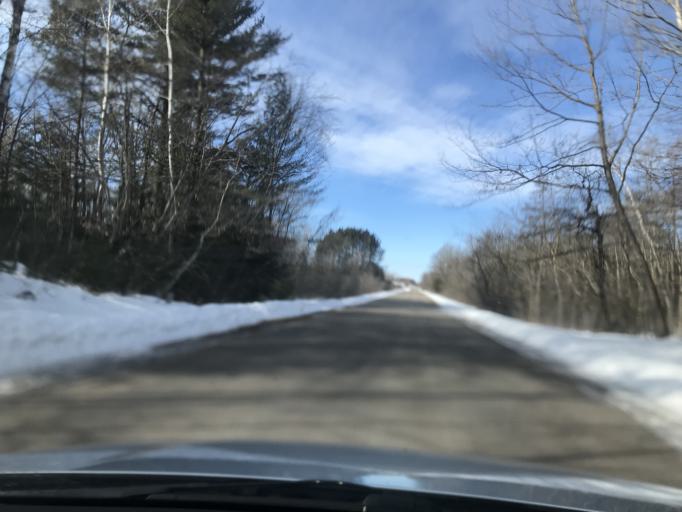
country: US
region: Wisconsin
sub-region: Oconto County
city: Gillett
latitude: 44.9617
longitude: -88.2816
